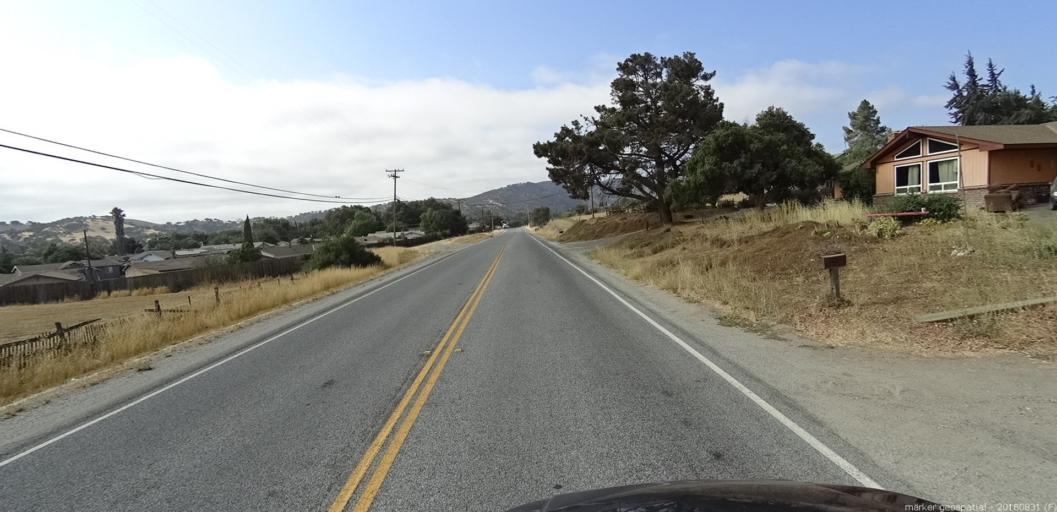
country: US
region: California
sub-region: Monterey County
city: King City
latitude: 36.1853
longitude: -121.1504
